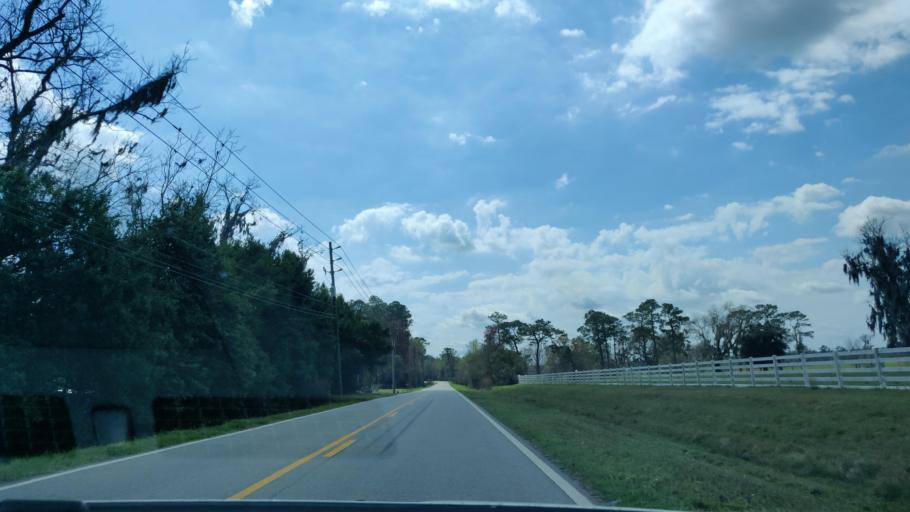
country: US
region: Florida
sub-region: Duval County
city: Baldwin
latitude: 30.2536
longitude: -81.9493
